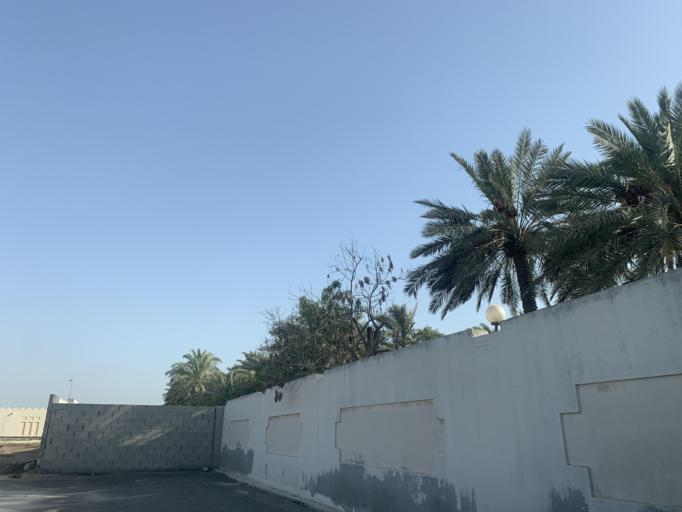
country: BH
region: Central Governorate
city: Madinat Hamad
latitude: 26.1914
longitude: 50.4577
